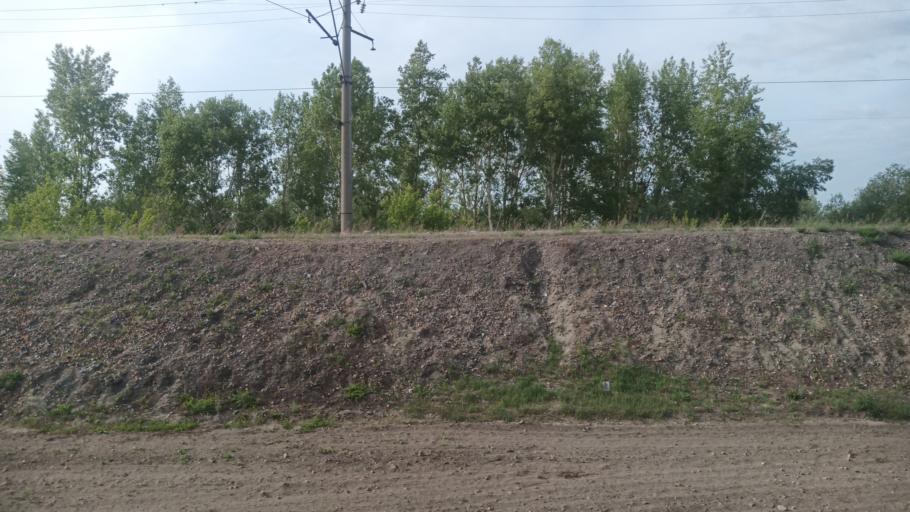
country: RU
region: Altai Krai
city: Novoaltaysk
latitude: 53.3692
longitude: 83.8578
